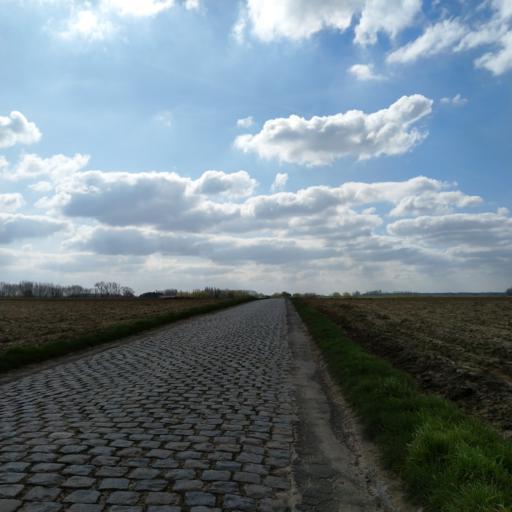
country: BE
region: Wallonia
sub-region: Province du Hainaut
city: Jurbise
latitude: 50.5527
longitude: 3.9507
